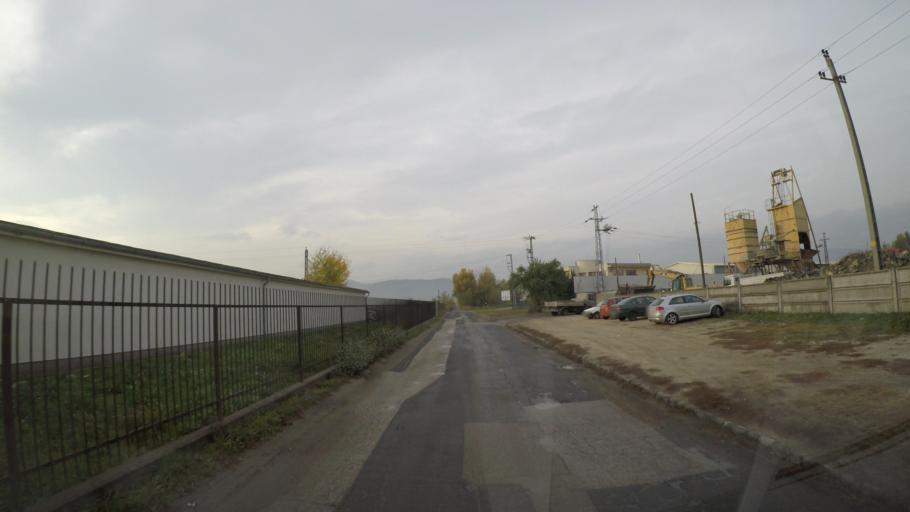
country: HU
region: Pest
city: Szentendre
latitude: 47.6566
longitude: 19.0642
